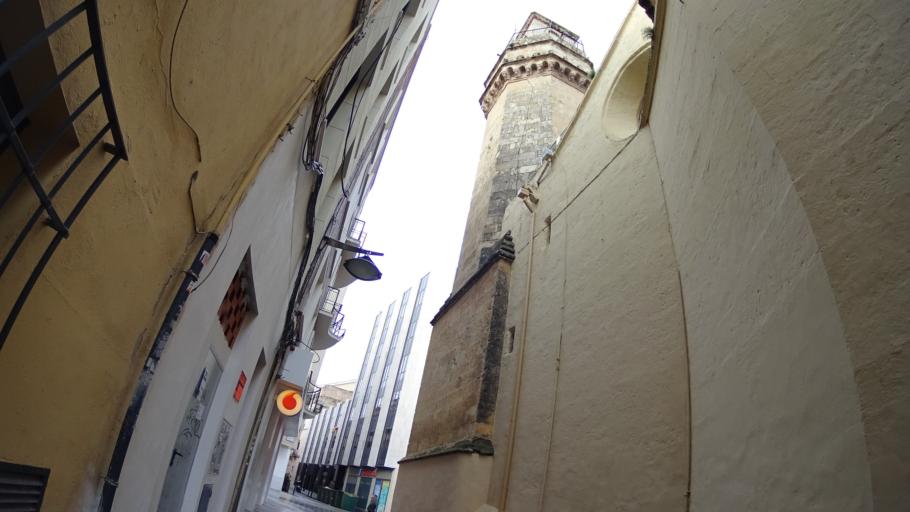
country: ES
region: Andalusia
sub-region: Province of Cordoba
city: Cordoba
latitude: 37.8845
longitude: -4.7824
